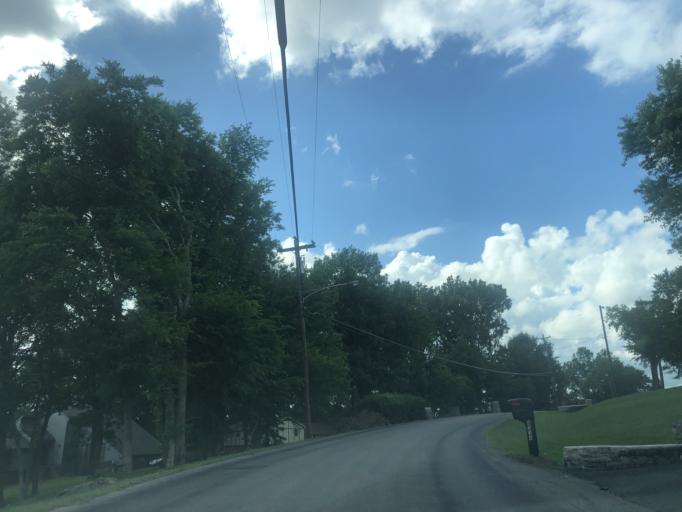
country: US
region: Tennessee
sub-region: Davidson County
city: Nashville
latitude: 36.2096
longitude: -86.8584
